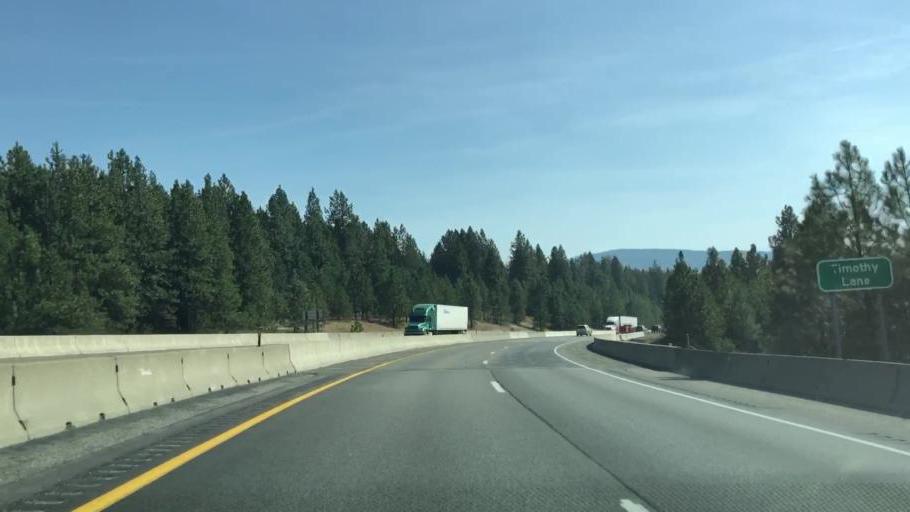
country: US
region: Idaho
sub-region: Kootenai County
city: Coeur d'Alene
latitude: 47.6387
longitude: -116.7079
